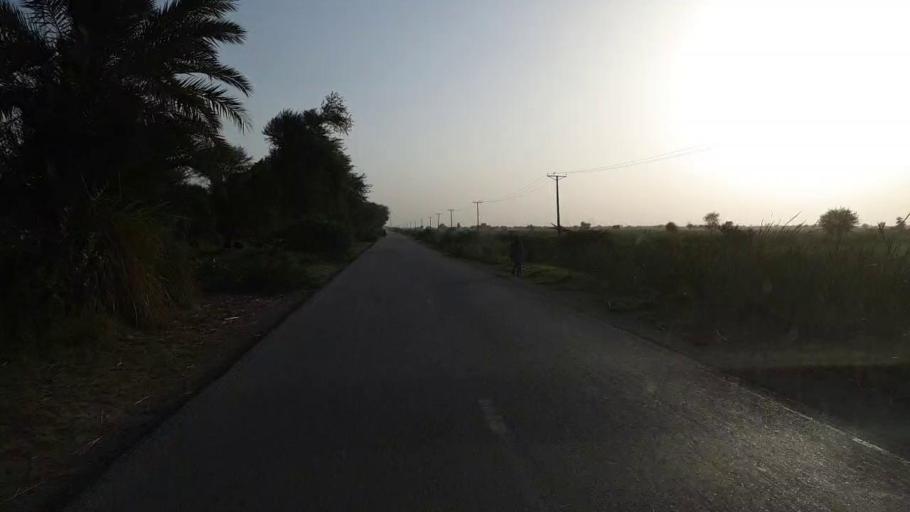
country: PK
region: Sindh
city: Jam Sahib
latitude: 26.2742
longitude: 68.5513
